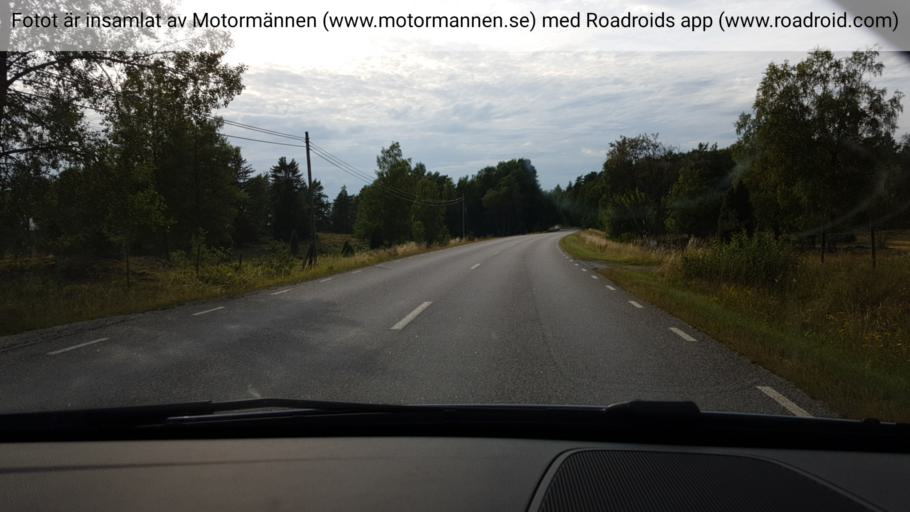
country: SE
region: Stockholm
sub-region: Norrtalje Kommun
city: Nykvarn
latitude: 59.9091
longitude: 18.2909
